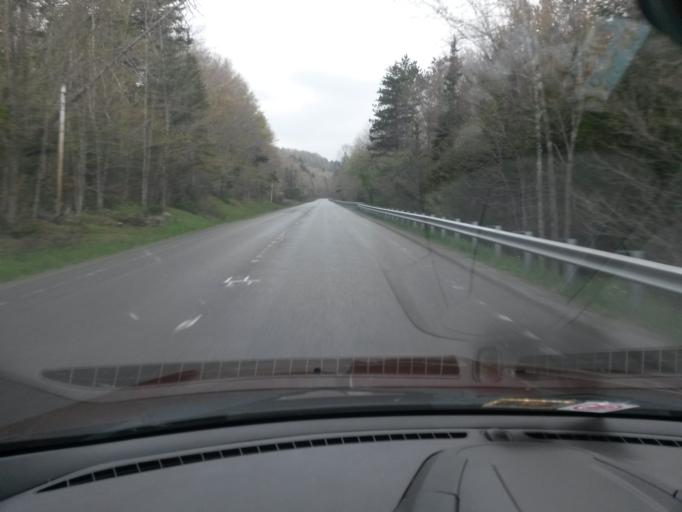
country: US
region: West Virginia
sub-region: Randolph County
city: Elkins
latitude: 38.6049
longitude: -79.8603
